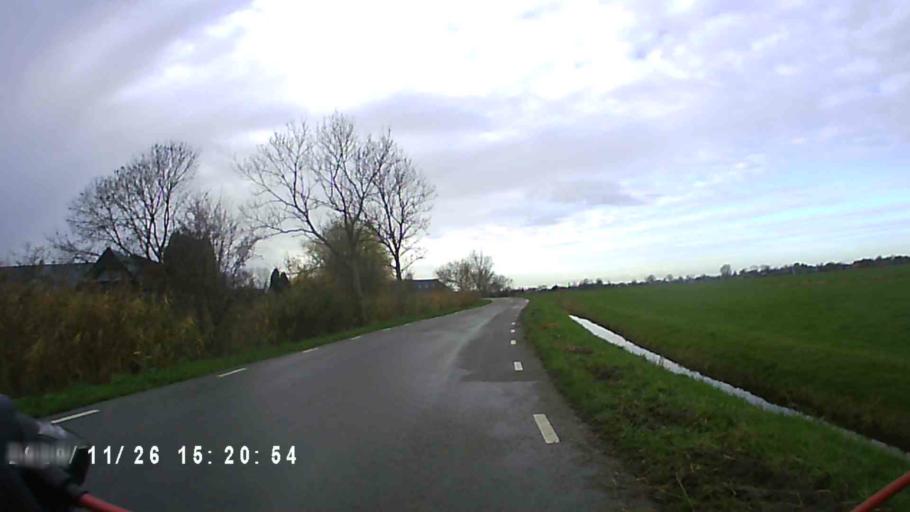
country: NL
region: Groningen
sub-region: Gemeente Appingedam
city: Appingedam
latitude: 53.3150
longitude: 6.7942
